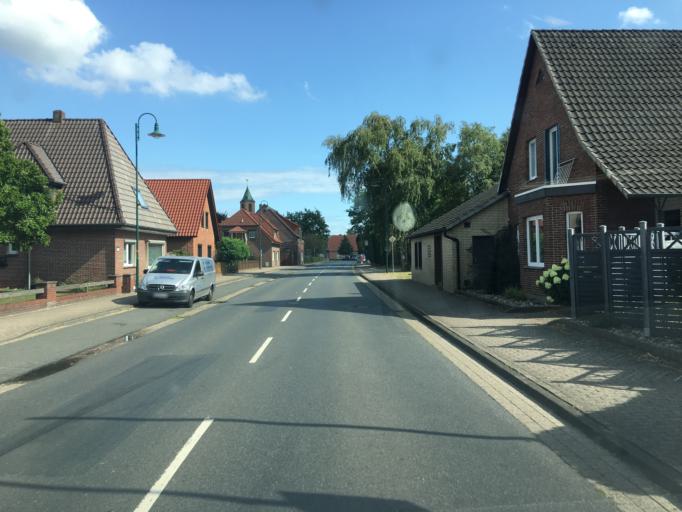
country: DE
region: Lower Saxony
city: Wardenburg
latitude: 53.0663
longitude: 8.1878
